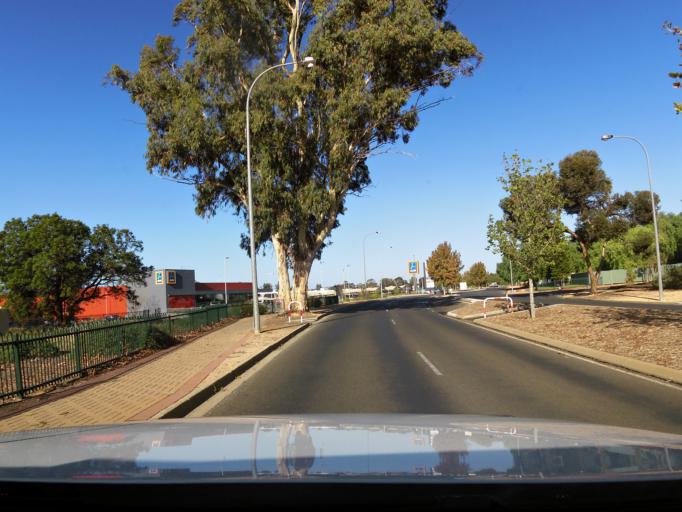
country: AU
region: South Australia
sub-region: Berri and Barmera
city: Berri
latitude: -34.2781
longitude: 140.6098
